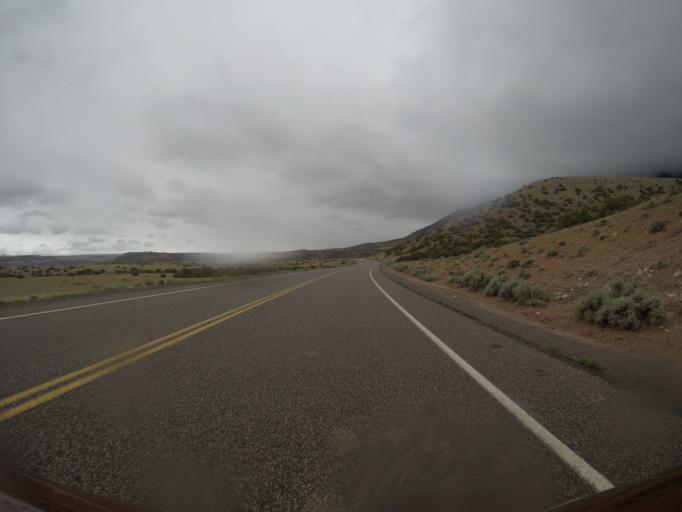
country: US
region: Wyoming
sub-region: Big Horn County
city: Lovell
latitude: 45.0697
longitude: -108.2548
